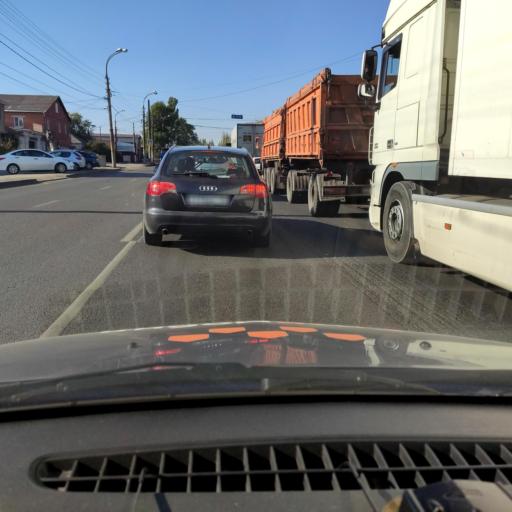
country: RU
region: Voronezj
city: Voronezh
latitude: 51.6429
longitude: 39.1546
